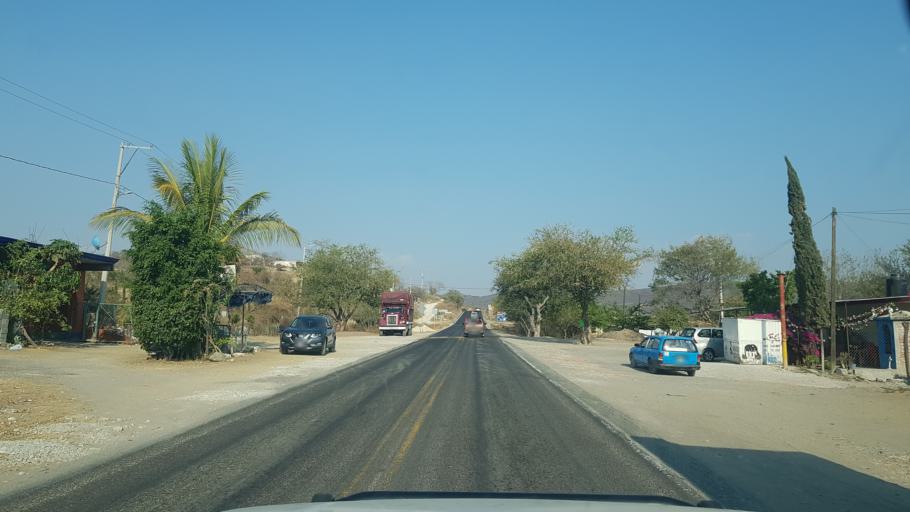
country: MX
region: Puebla
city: Calmeca
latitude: 18.6433
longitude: -98.6287
